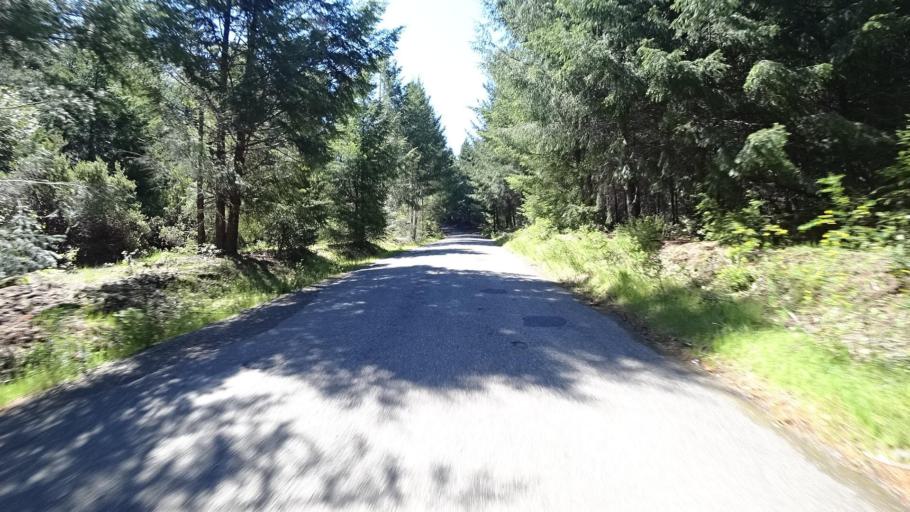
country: US
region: California
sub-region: Humboldt County
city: Redway
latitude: 40.1614
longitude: -124.0802
